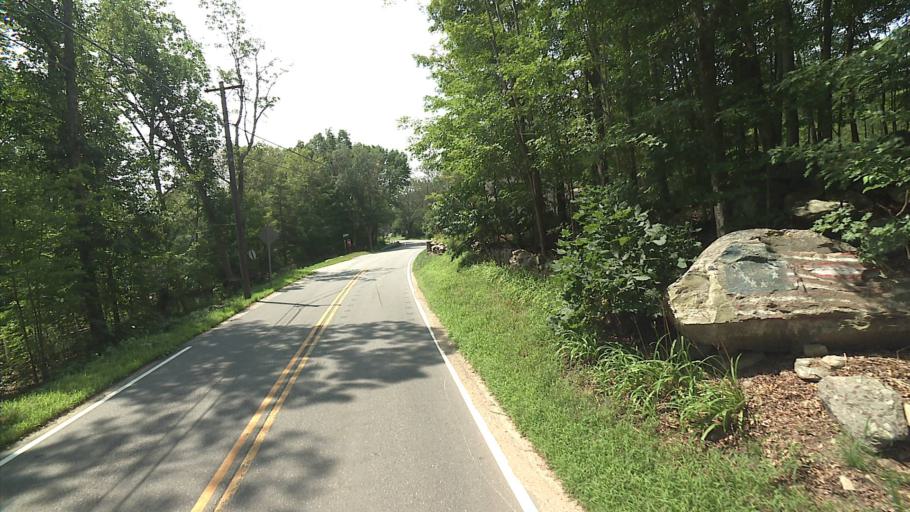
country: US
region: Connecticut
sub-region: Windham County
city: Moosup
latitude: 41.7404
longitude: -71.8553
